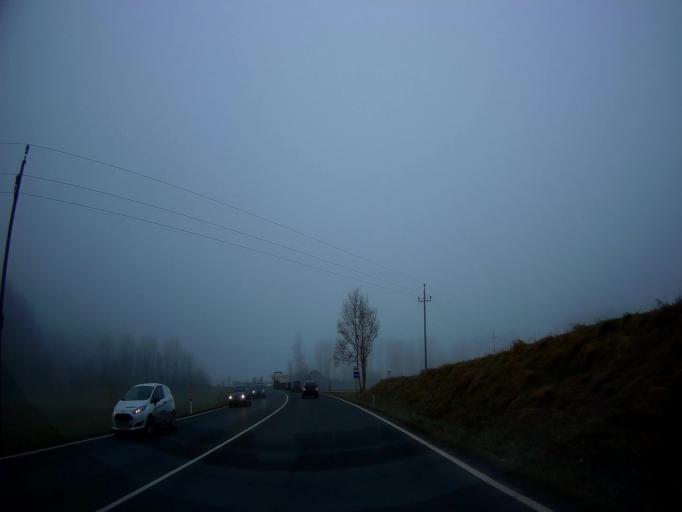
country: AT
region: Salzburg
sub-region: Politischer Bezirk Zell am See
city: Maishofen
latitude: 47.3948
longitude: 12.8005
